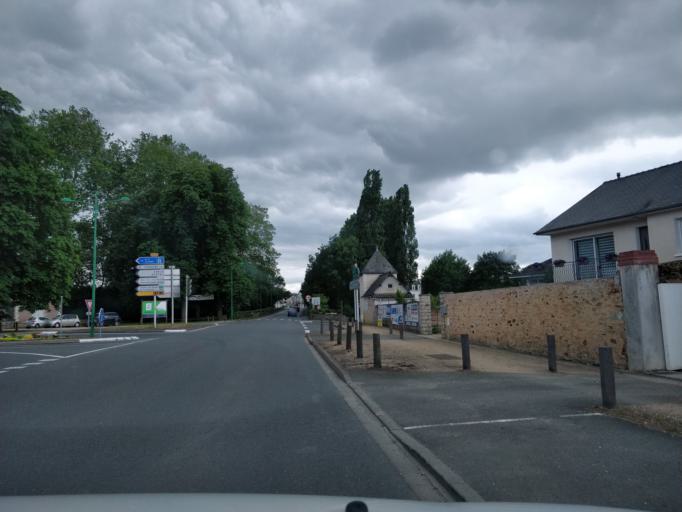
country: FR
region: Pays de la Loire
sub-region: Departement de Maine-et-Loire
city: Grez-Neuville
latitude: 47.6311
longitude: -0.7113
